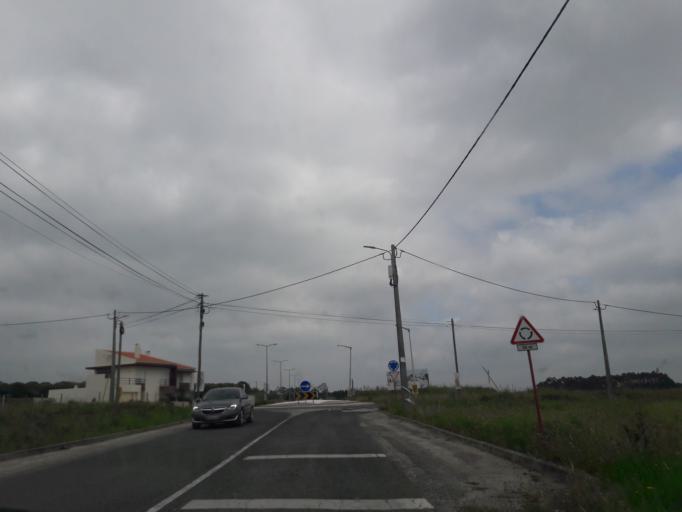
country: PT
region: Leiria
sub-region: Peniche
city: Atouguia da Baleia
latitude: 39.3385
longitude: -9.2742
